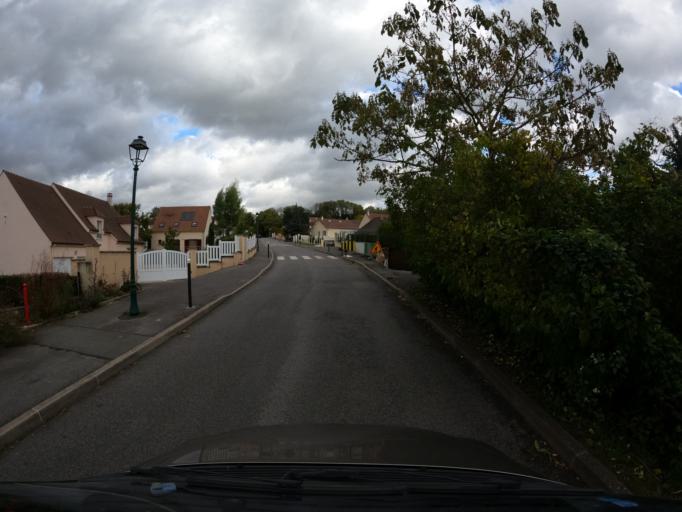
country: FR
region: Ile-de-France
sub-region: Departement de Seine-et-Marne
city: Coupvray
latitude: 48.8981
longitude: 2.7922
